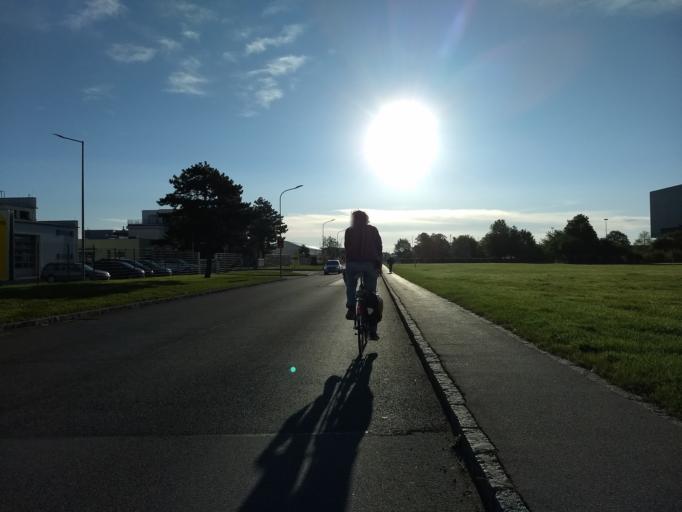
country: AT
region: Lower Austria
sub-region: Politischer Bezirk Modling
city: Wiener Neudorf
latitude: 48.0754
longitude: 16.3195
